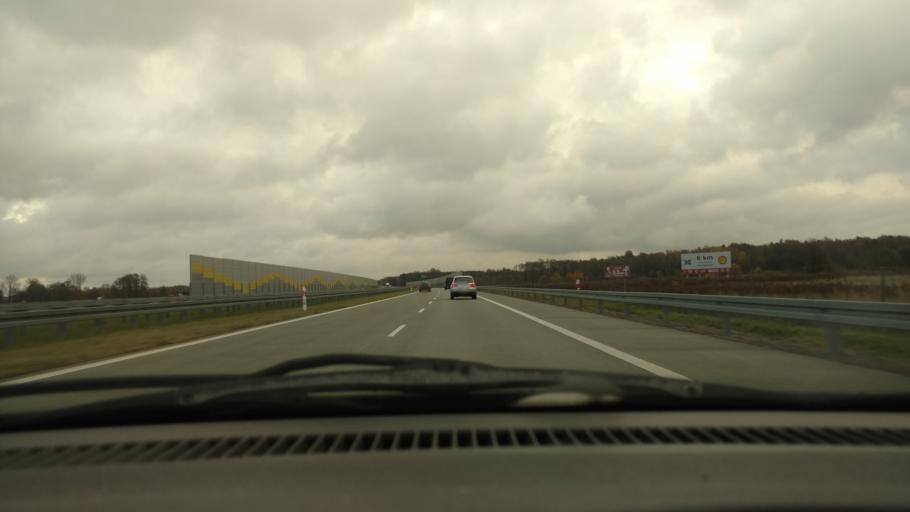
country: PL
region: Lodz Voivodeship
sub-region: Powiat lodzki wschodni
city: Rzgow
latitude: 51.6328
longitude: 19.4568
